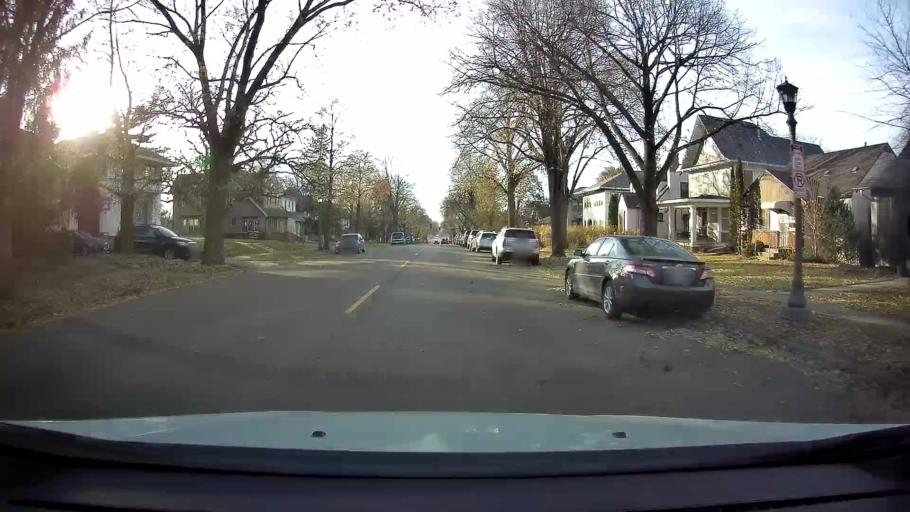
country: US
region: Minnesota
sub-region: Dakota County
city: West Saint Paul
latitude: 44.9342
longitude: -93.1444
